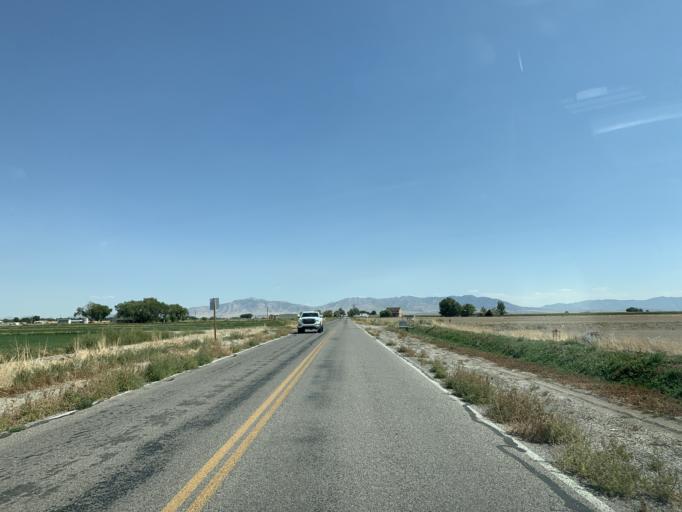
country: US
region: Utah
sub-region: Millard County
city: Delta
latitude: 39.3378
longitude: -112.6111
